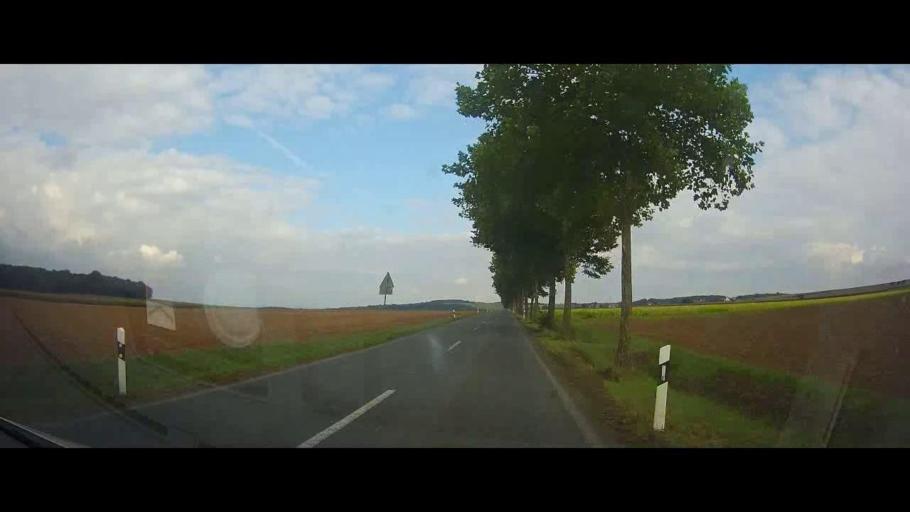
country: DE
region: Lower Saxony
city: Adelebsen
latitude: 51.5624
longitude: 9.8208
